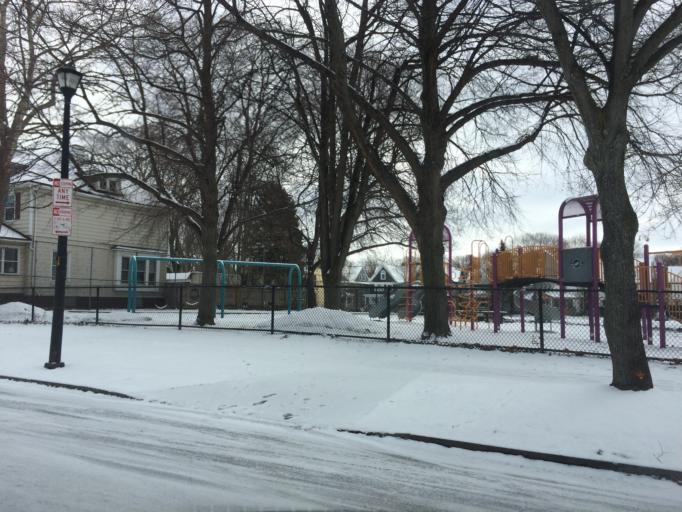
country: US
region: New York
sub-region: Monroe County
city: Rochester
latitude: 43.1394
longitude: -77.5884
